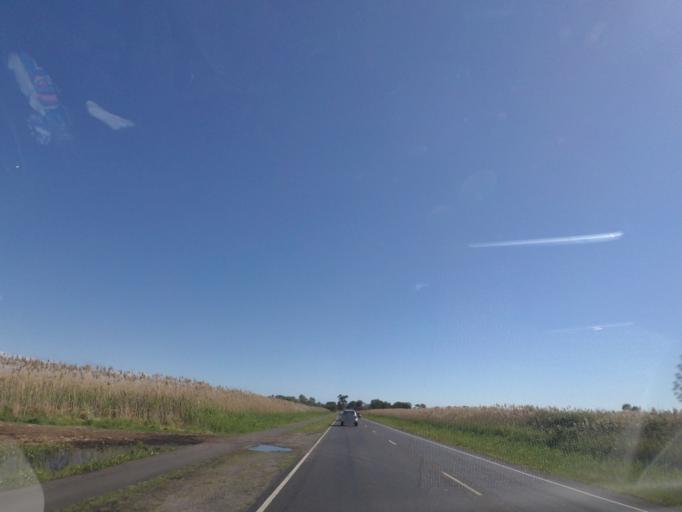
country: AU
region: Victoria
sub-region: Kingston
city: Chelsea Heights
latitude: -38.0315
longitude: 145.1264
